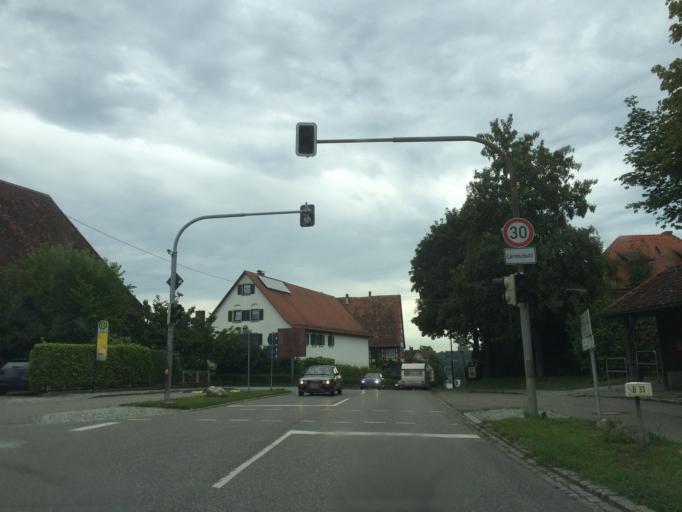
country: DE
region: Baden-Wuerttemberg
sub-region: Tuebingen Region
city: Hagnau
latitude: 47.7009
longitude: 9.3392
